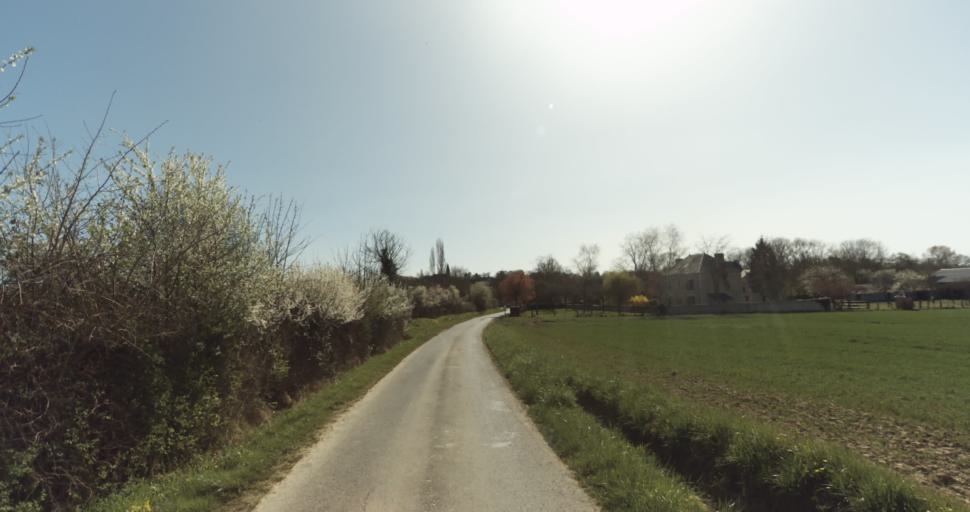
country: FR
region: Lower Normandy
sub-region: Departement du Calvados
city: Saint-Pierre-sur-Dives
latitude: 48.9484
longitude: -0.0046
